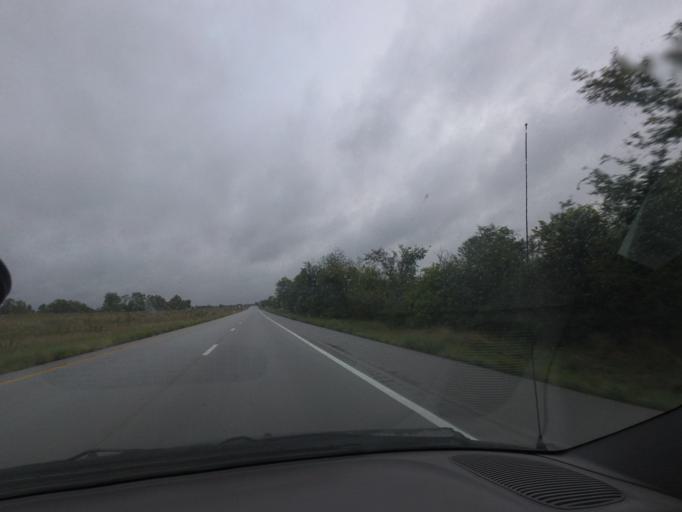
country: US
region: Missouri
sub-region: Marion County
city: Monroe City
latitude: 39.6671
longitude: -91.6721
